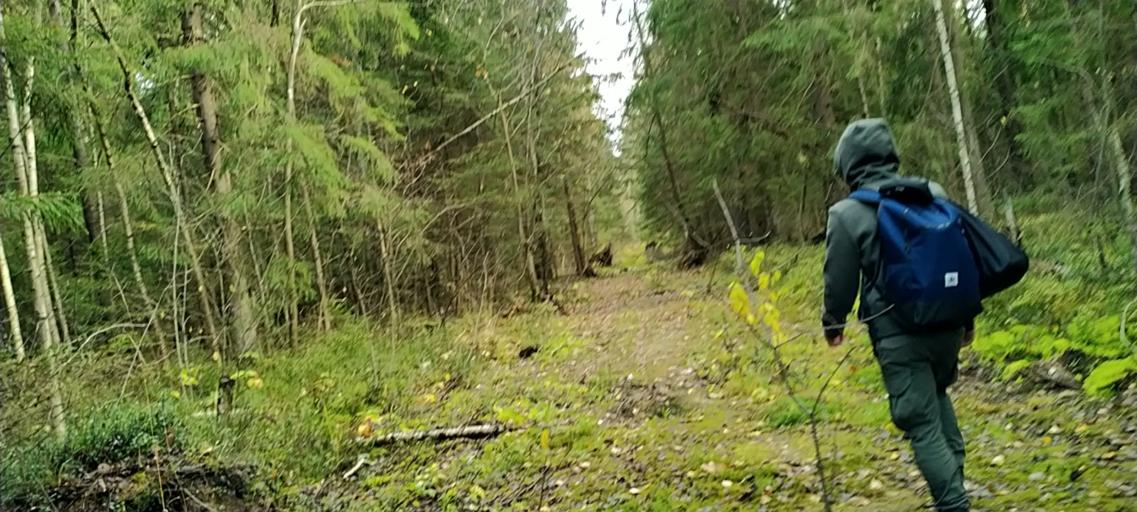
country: RU
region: Moskovskaya
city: Davydovo
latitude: 55.5605
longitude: 38.7926
